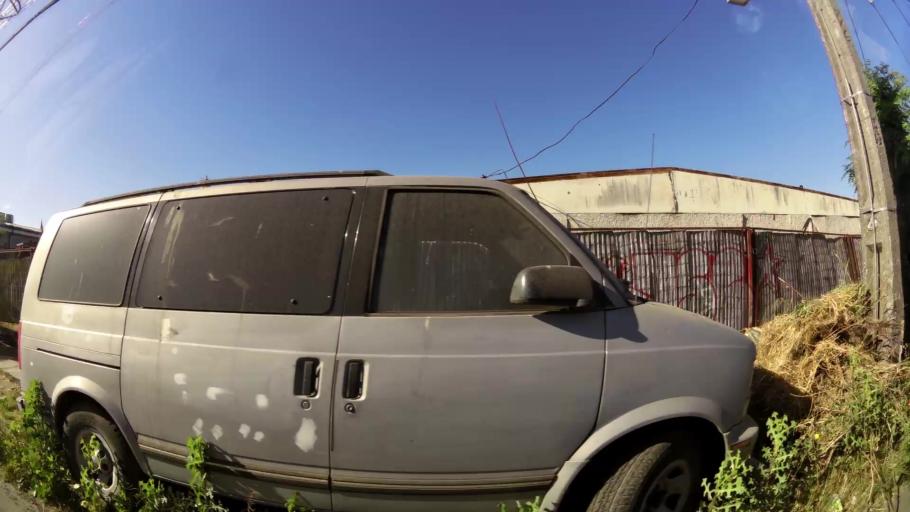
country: CL
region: Santiago Metropolitan
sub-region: Provincia de Maipo
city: San Bernardo
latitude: -33.5400
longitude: -70.6791
